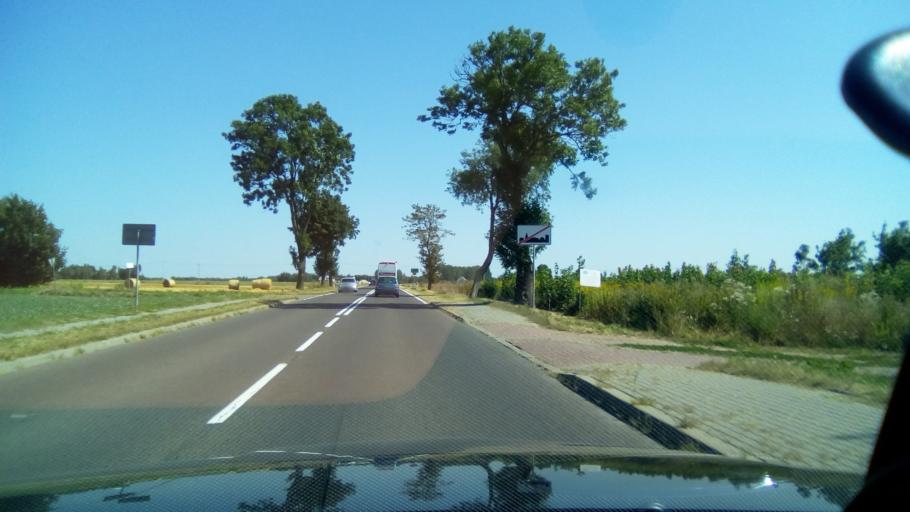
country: PL
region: Masovian Voivodeship
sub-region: Powiat plocki
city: Starozreby
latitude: 52.6353
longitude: 20.0023
